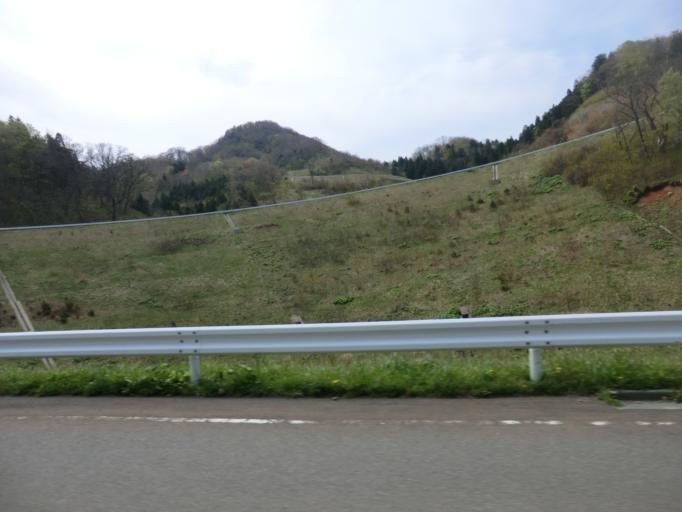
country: JP
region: Aomori
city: Mutsu
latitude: 41.3657
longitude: 140.8310
